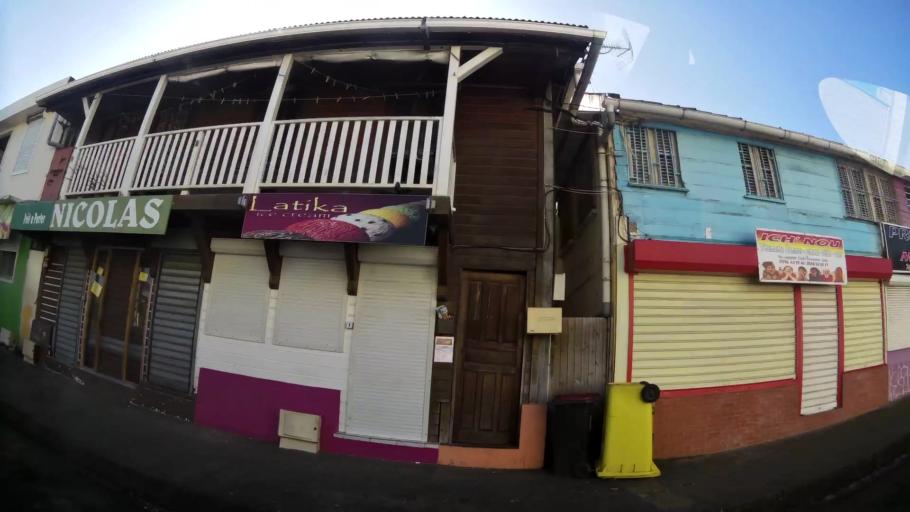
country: MQ
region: Martinique
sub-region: Martinique
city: Le Francois
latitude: 14.6161
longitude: -60.9019
